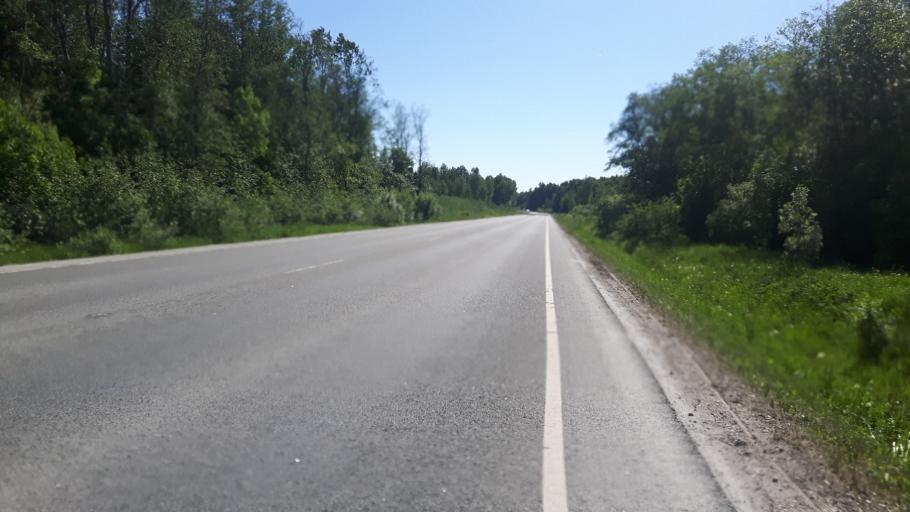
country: EE
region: Raplamaa
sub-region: Rapla vald
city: Rapla
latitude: 59.0284
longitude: 24.8189
